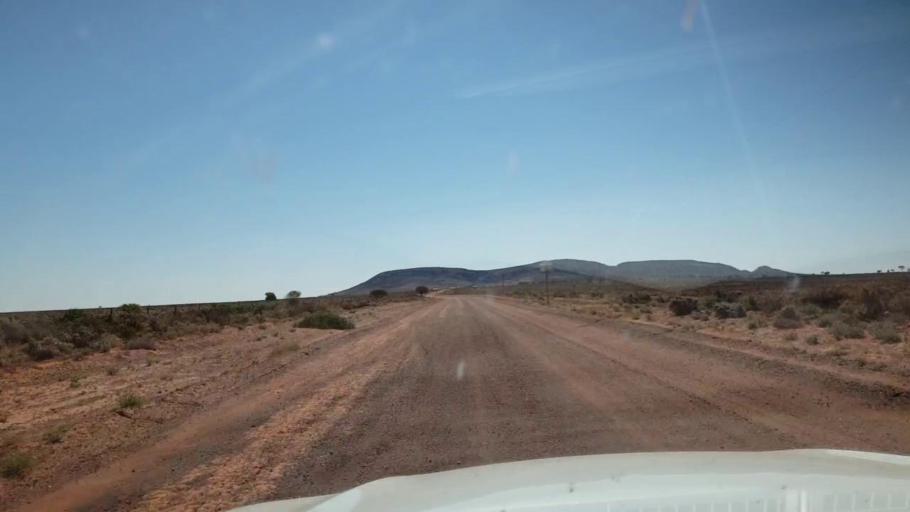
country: AU
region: South Australia
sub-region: Whyalla
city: Whyalla
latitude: -32.7122
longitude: 137.1413
